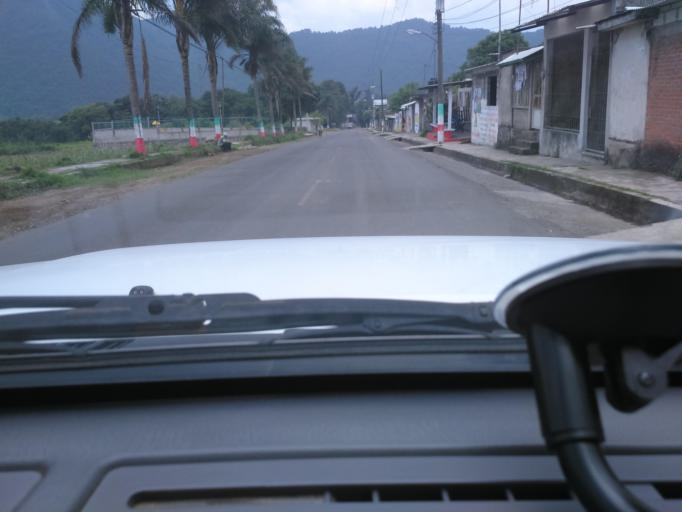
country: MX
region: Veracruz
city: Atzacan
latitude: 18.8909
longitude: -97.0905
